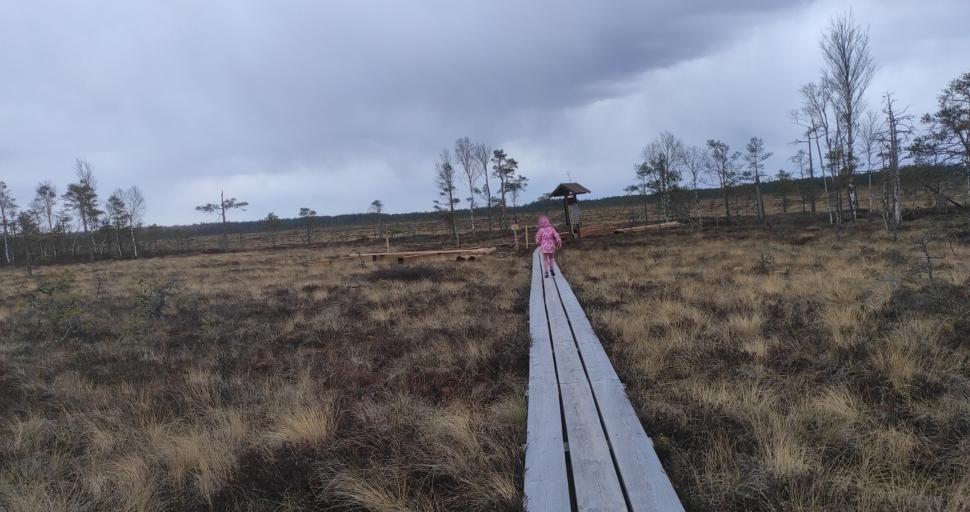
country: LV
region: Dundaga
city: Dundaga
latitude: 57.3445
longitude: 22.1565
